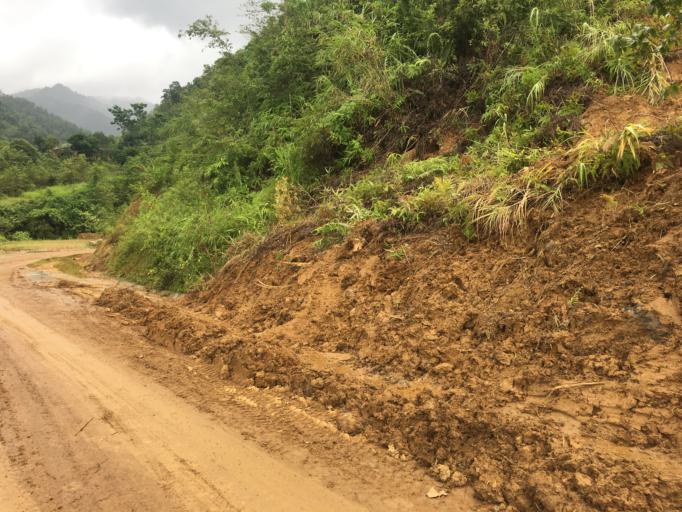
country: VN
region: Ha Giang
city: Thi Tran Tam Son
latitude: 22.9941
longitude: 105.0752
